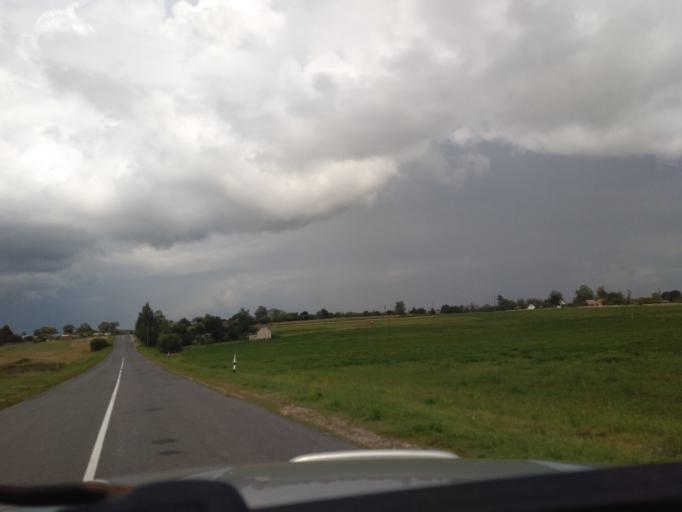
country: BY
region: Minsk
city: Tsimkavichy
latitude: 53.0600
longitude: 26.9872
